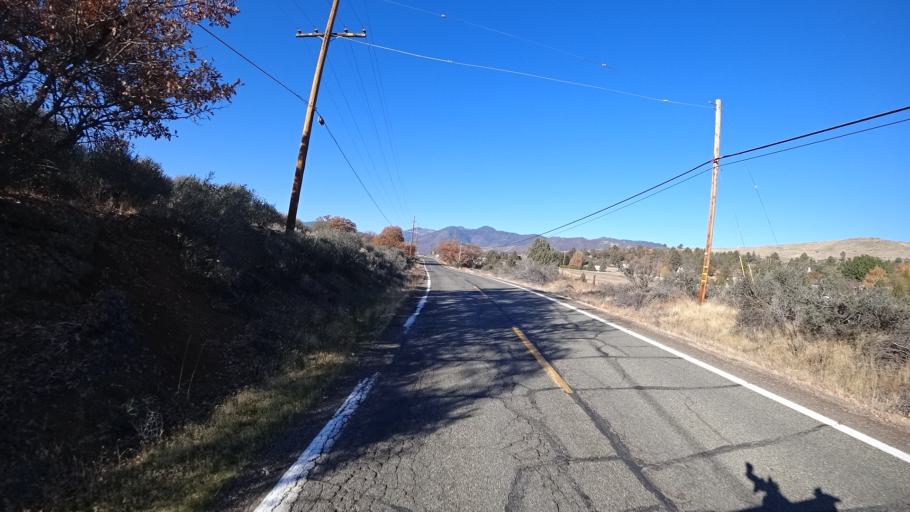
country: US
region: California
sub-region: Siskiyou County
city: Yreka
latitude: 41.7390
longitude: -122.6112
